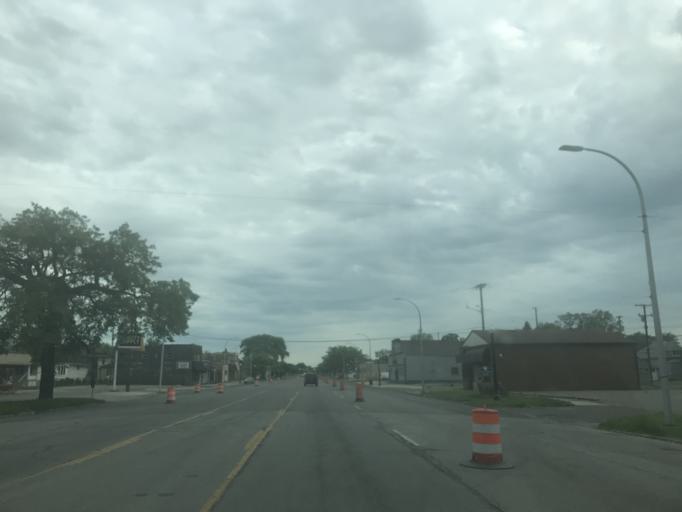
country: US
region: Michigan
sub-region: Wayne County
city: River Rouge
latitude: 42.2618
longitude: -83.1375
